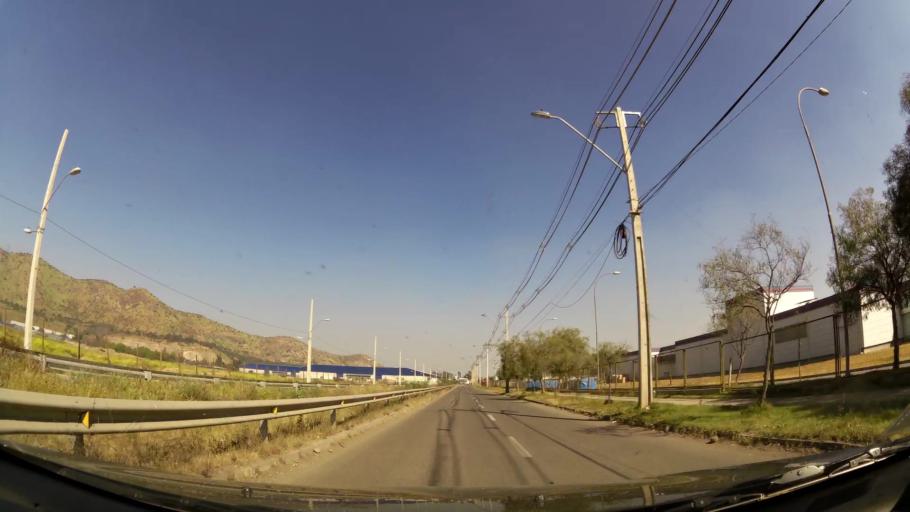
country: CL
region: Santiago Metropolitan
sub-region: Provincia de Chacabuco
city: Chicureo Abajo
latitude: -33.3373
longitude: -70.7032
